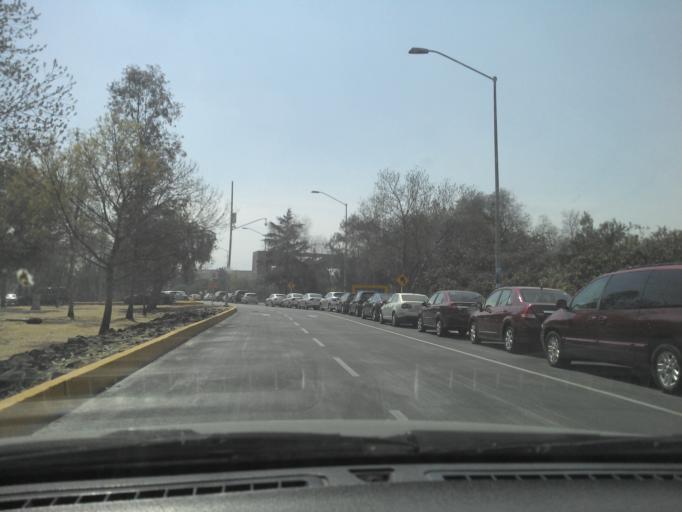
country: MX
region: Mexico City
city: Tlalpan
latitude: 19.3135
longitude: -99.1862
